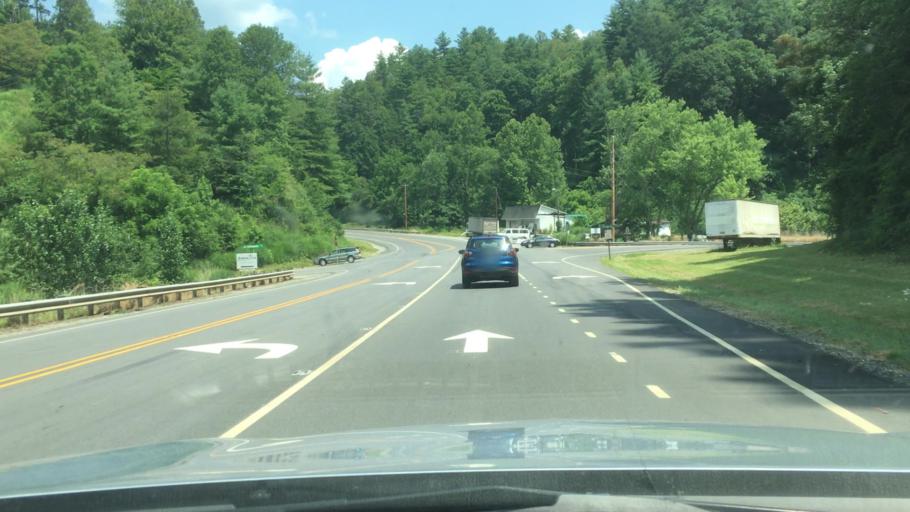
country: US
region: North Carolina
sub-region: Madison County
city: Mars Hill
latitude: 35.8230
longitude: -82.6127
